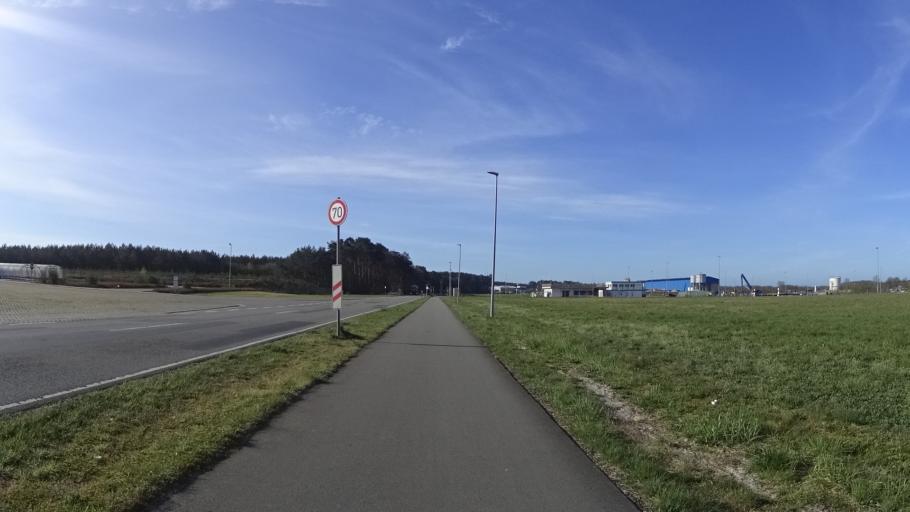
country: DE
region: Lower Saxony
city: Haren
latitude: 52.7782
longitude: 7.2781
